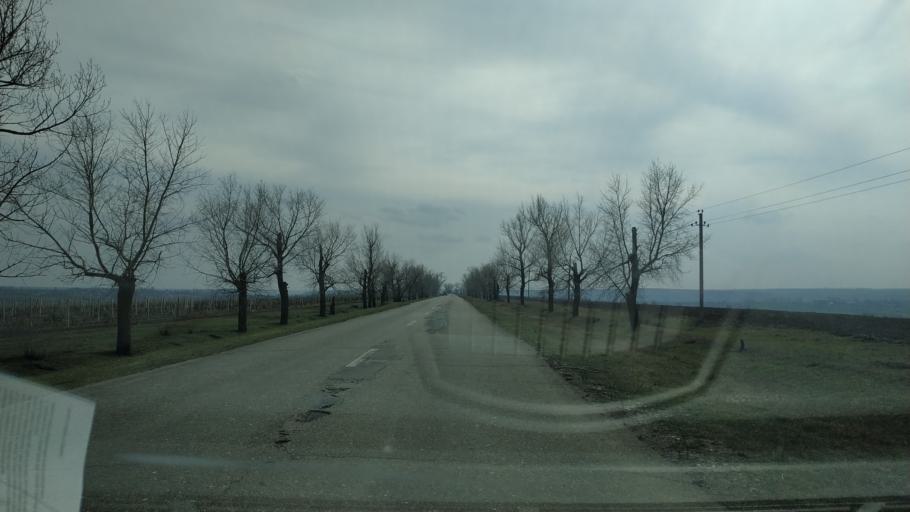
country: MD
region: Gagauzia
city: Vulcanesti
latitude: 45.7098
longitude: 28.4005
